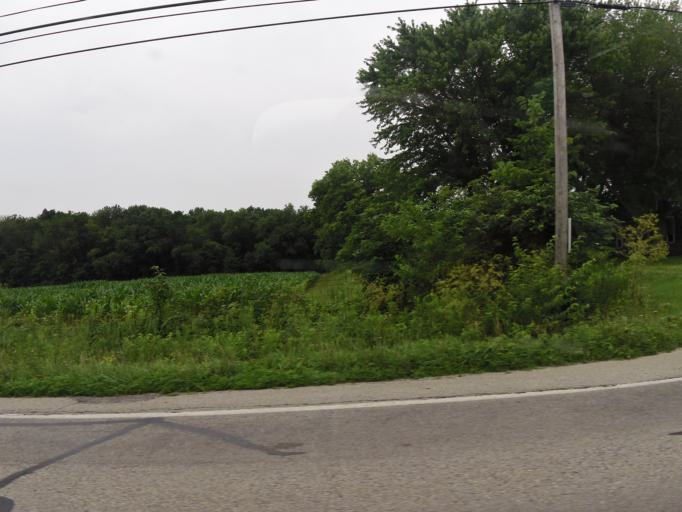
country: US
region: Ohio
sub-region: Clinton County
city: Wilmington
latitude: 39.4824
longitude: -83.9139
